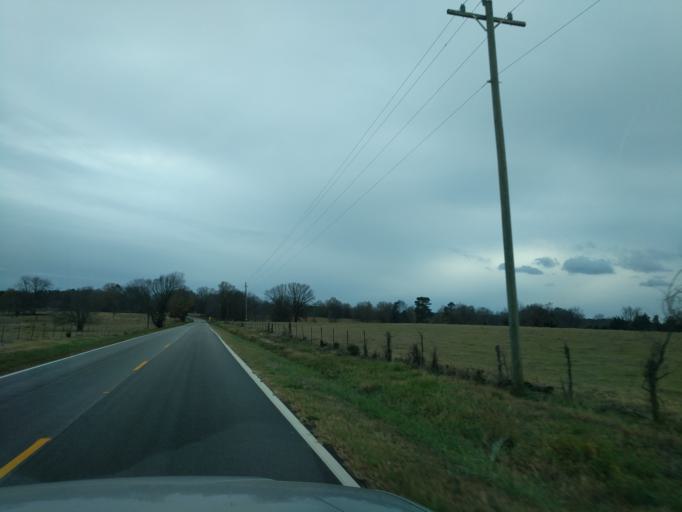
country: US
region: South Carolina
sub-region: Laurens County
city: Laurens
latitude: 34.3512
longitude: -81.9910
